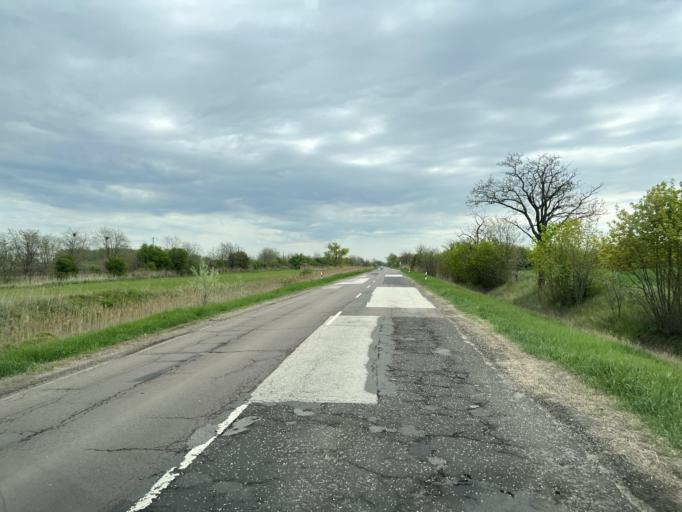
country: HU
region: Pest
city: Cegled
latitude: 47.1811
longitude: 19.8795
